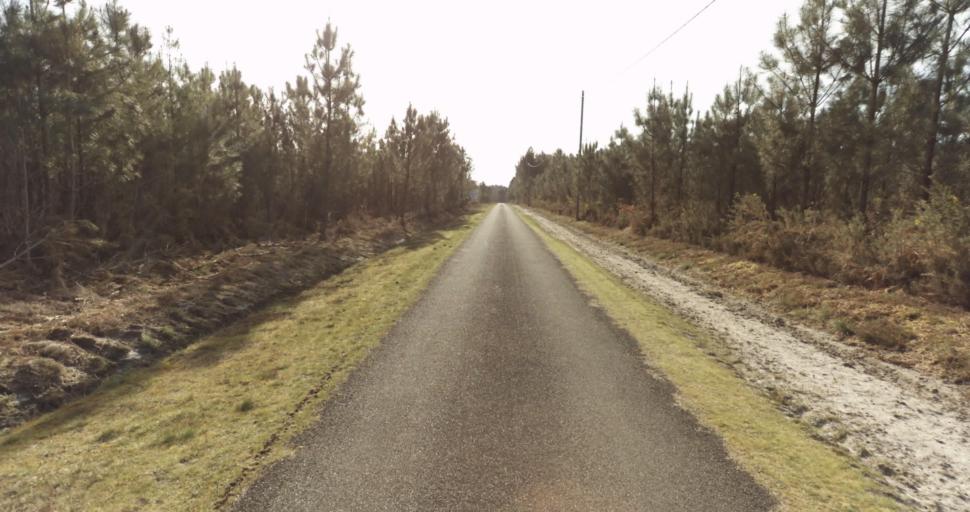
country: FR
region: Aquitaine
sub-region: Departement des Landes
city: Roquefort
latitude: 44.1238
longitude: -0.3074
